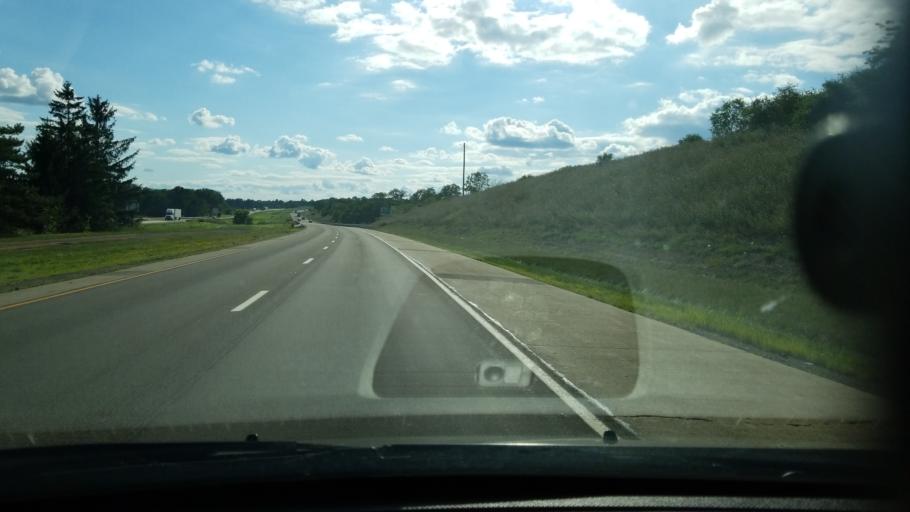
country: US
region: Pennsylvania
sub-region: Northumberland County
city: Riverside
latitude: 40.9900
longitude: -76.6799
